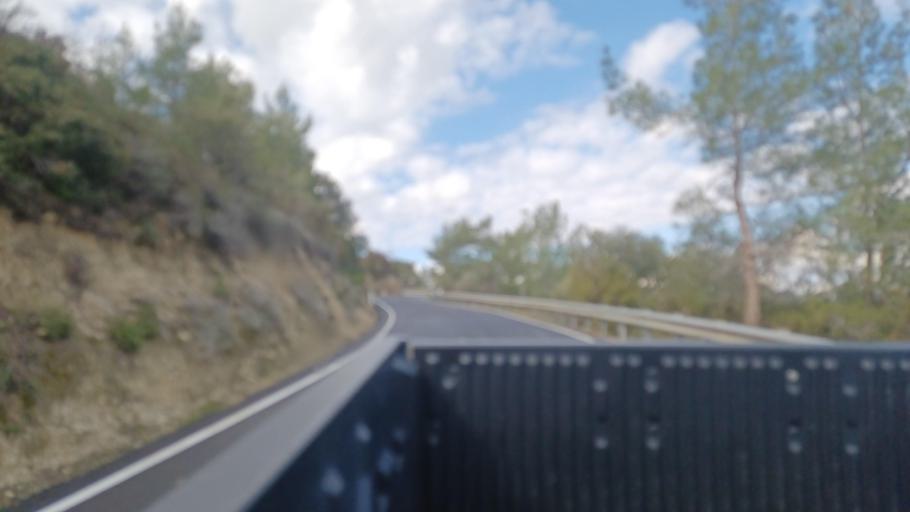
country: CY
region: Limassol
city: Pissouri
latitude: 34.7464
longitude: 32.6624
